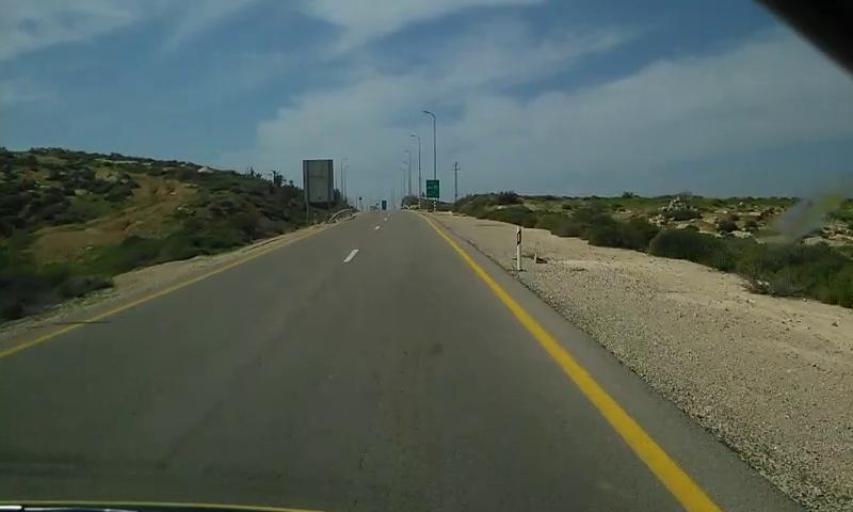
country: PS
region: West Bank
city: Az Zahiriyah
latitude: 31.3749
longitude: 35.0094
